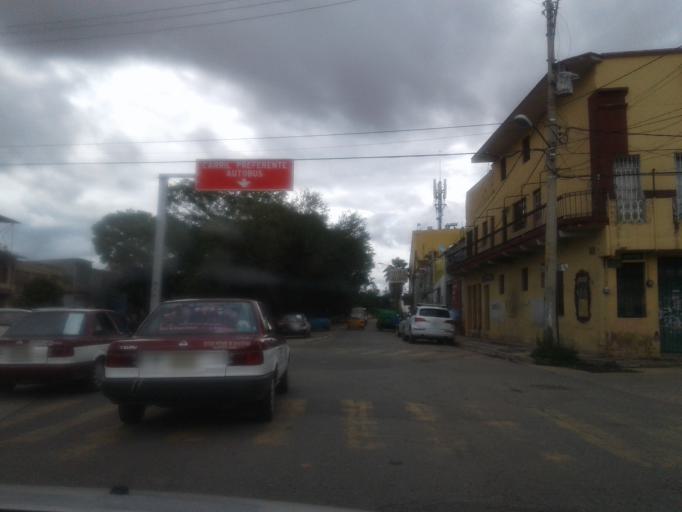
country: MX
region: Oaxaca
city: Oaxaca de Juarez
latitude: 17.0638
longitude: -96.7356
